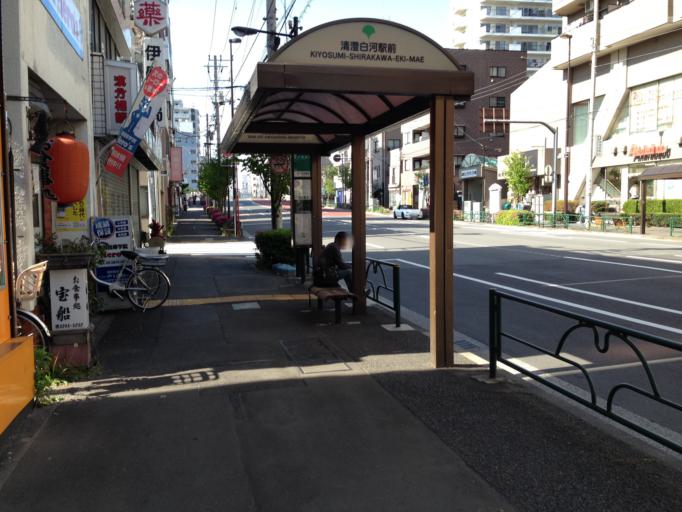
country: JP
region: Tokyo
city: Urayasu
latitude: 35.6823
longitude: 139.7988
